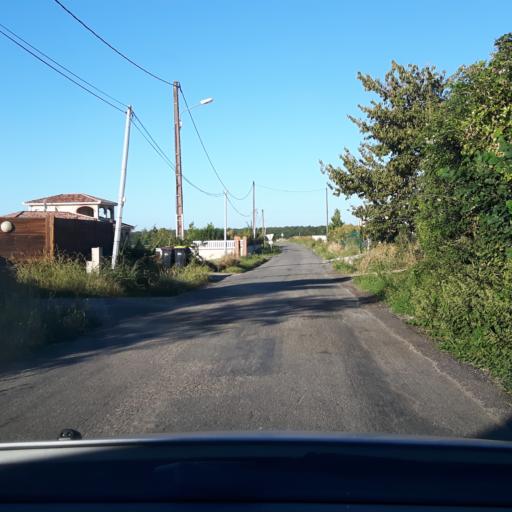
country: FR
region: Midi-Pyrenees
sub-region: Departement de la Haute-Garonne
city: Castelnau-d'Estretefonds
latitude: 43.7942
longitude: 1.3680
